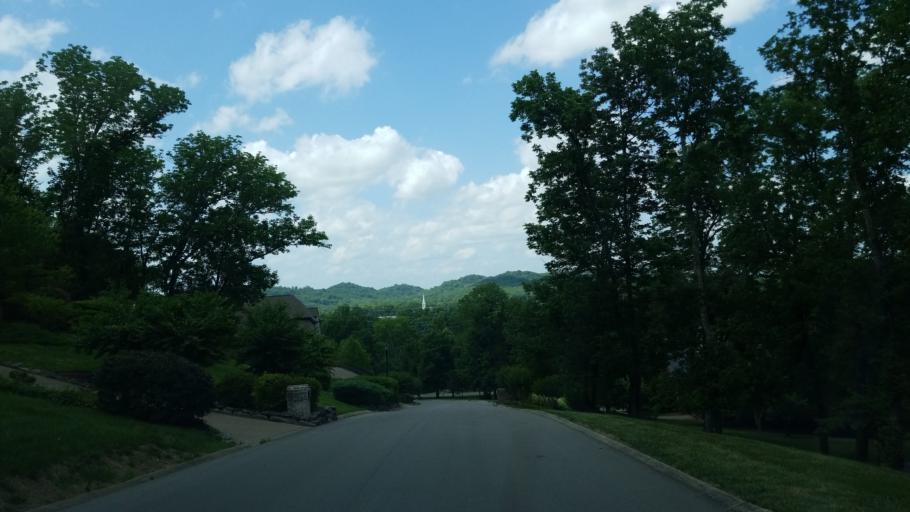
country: US
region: Tennessee
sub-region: Davidson County
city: Forest Hills
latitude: 36.0385
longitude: -86.8644
